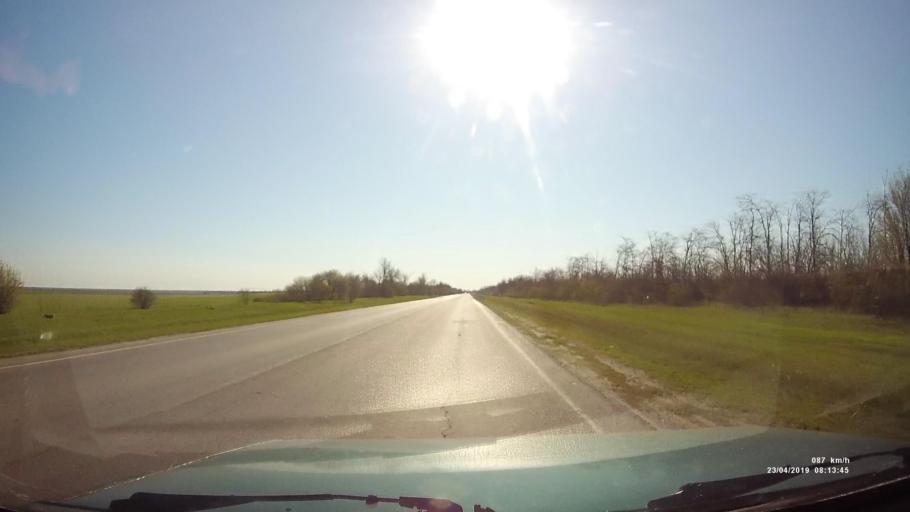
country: RU
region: Rostov
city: Yegorlykskaya
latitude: 46.5479
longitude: 40.7431
